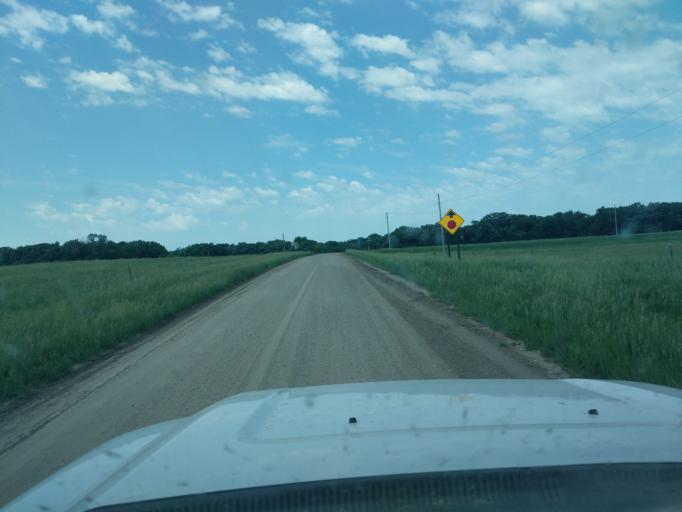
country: US
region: Minnesota
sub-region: Yellow Medicine County
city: Granite Falls
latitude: 44.7453
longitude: -95.3998
